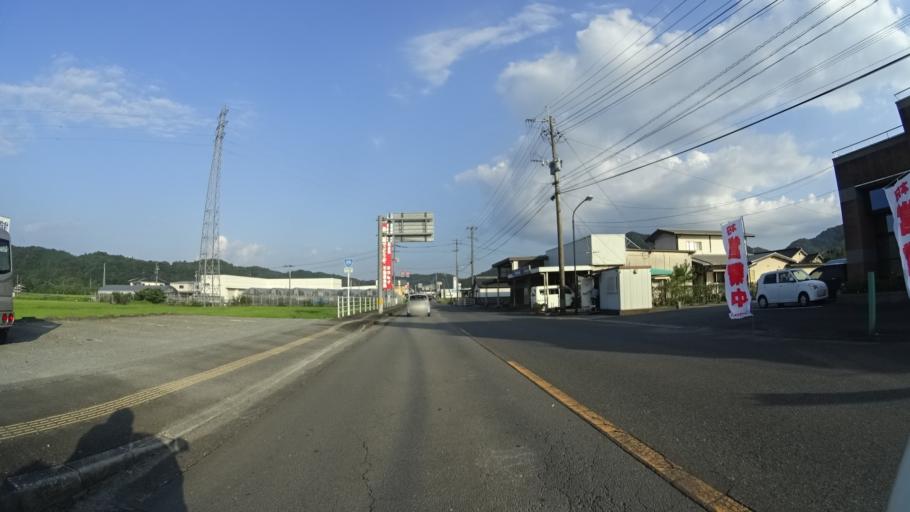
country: JP
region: Oita
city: Bungo-Takada-shi
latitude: 33.4374
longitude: 131.3590
